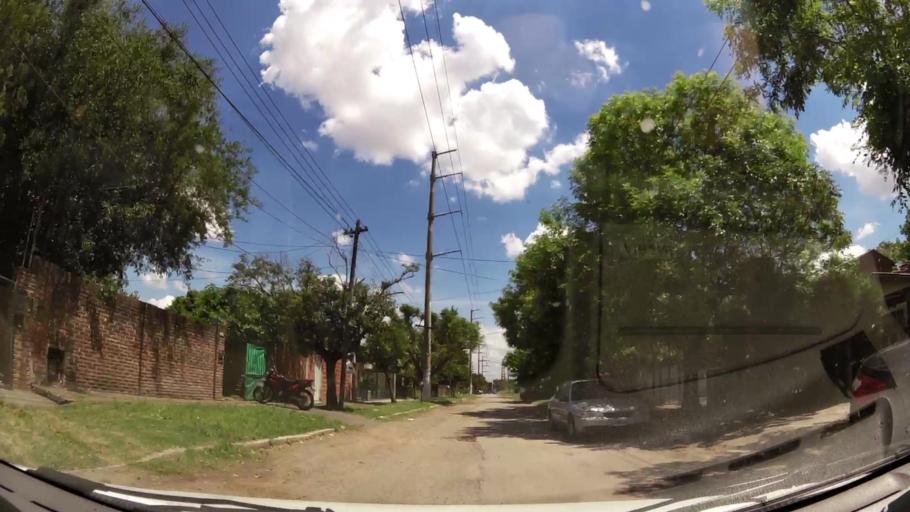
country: AR
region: Buenos Aires
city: Ituzaingo
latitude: -34.6446
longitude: -58.6872
